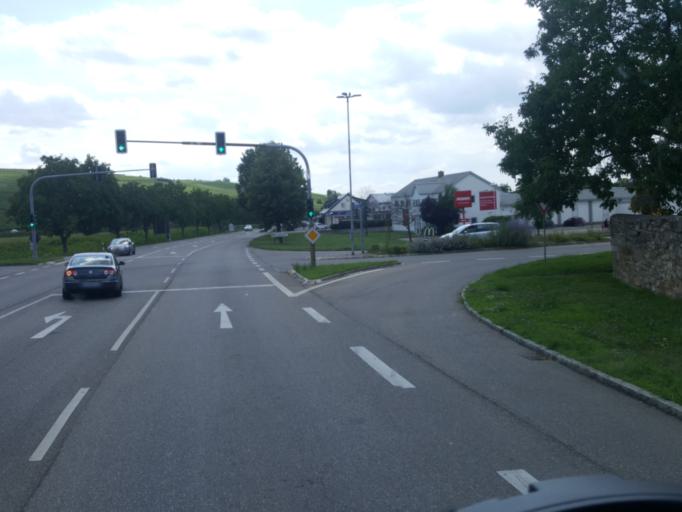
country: DE
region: Baden-Wuerttemberg
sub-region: Freiburg Region
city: Mullheim
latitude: 47.8090
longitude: 7.6082
